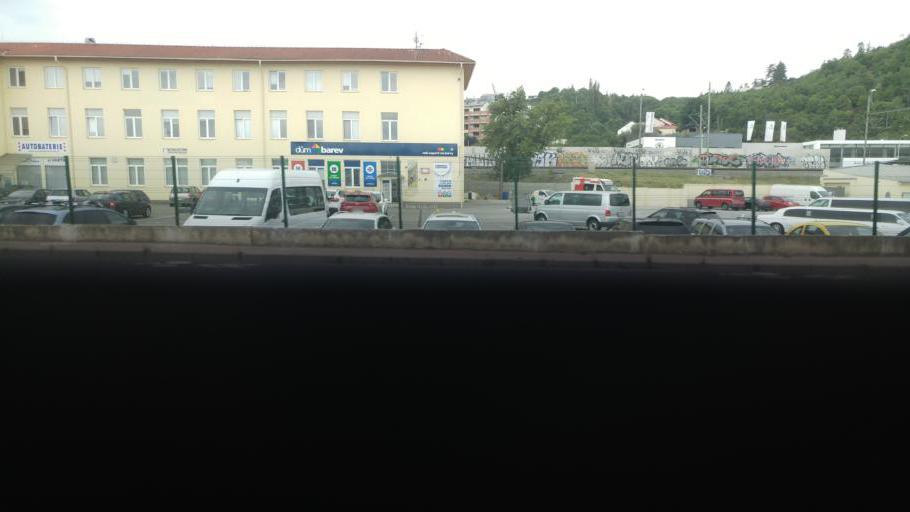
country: CZ
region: Praha
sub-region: Praha 1
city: Mala Strana
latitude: 50.1145
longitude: 14.3939
